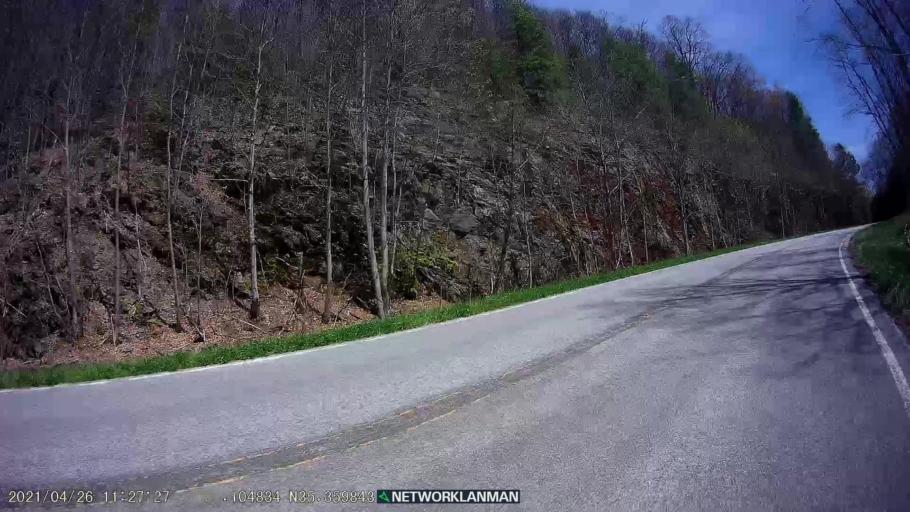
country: US
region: Tennessee
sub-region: Monroe County
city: Vonore
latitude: 35.3597
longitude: -84.1046
